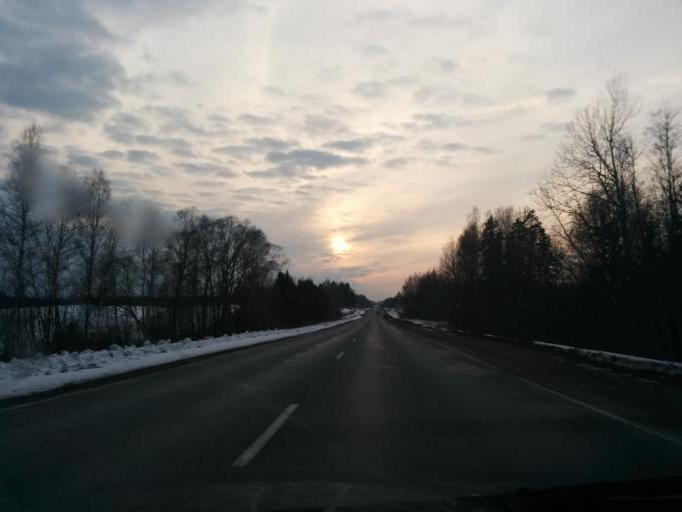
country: LV
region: Raunas
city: Rauna
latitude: 57.3095
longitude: 25.6351
